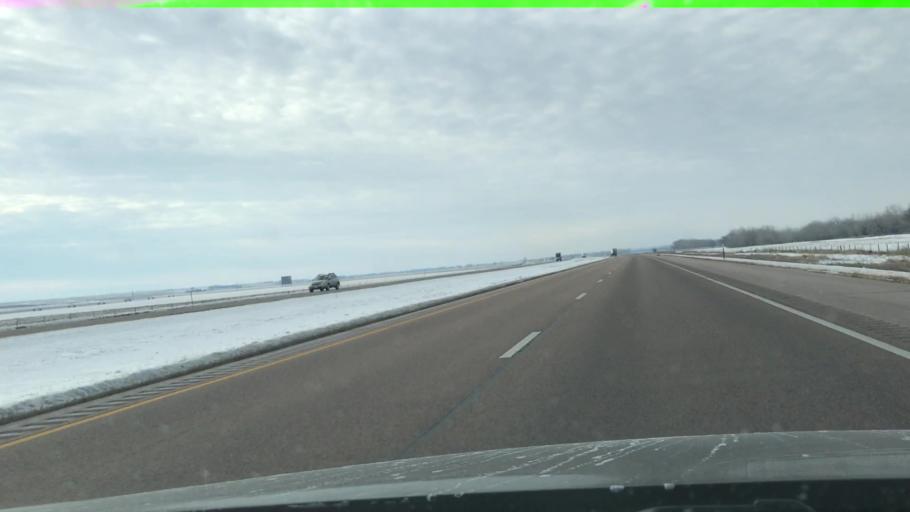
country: US
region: Nebraska
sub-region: Keith County
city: Ogallala
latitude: 41.1201
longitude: -101.6151
